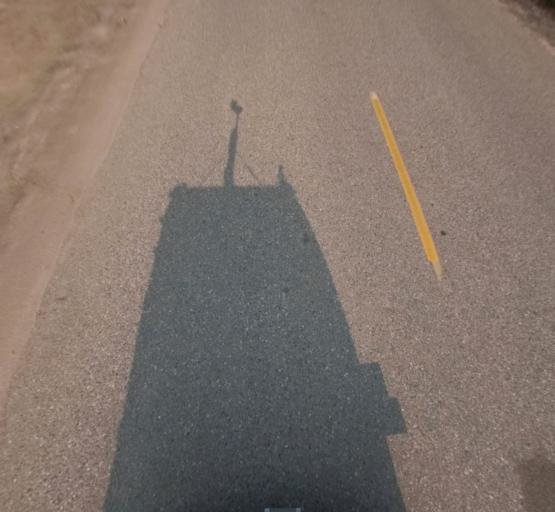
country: US
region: California
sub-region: Madera County
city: Madera Acres
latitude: 37.0162
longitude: -120.0572
